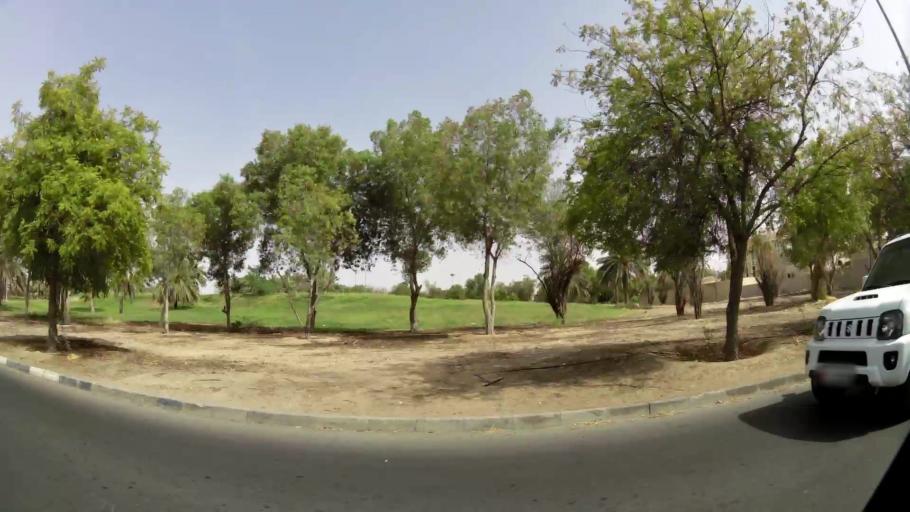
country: AE
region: Abu Dhabi
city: Al Ain
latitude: 24.1878
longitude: 55.6353
